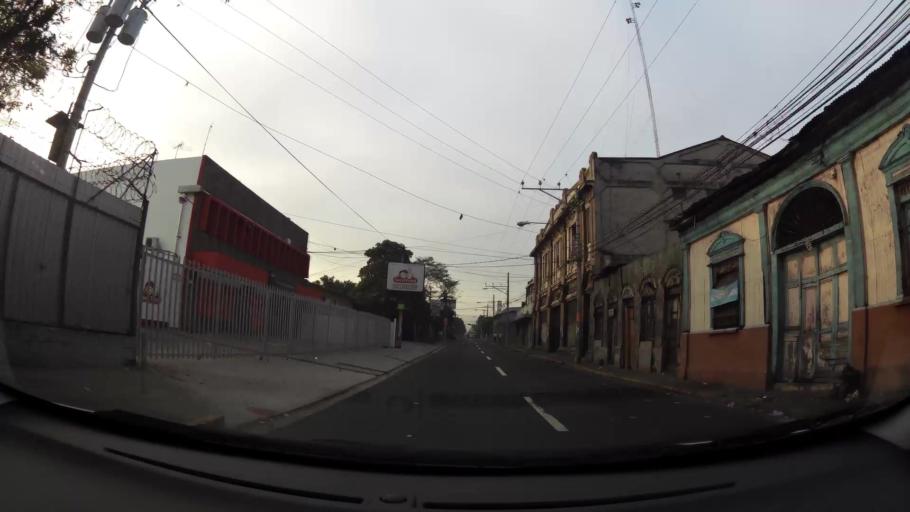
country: SV
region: San Salvador
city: San Salvador
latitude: 13.7042
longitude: -89.1909
